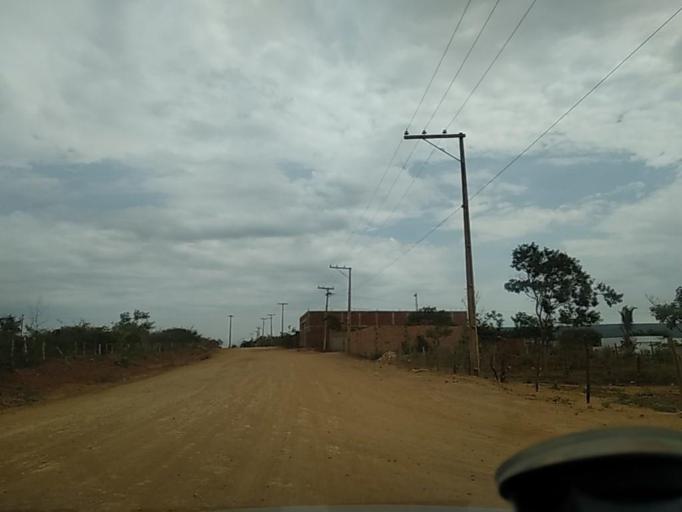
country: BR
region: Bahia
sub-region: Caetite
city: Caetite
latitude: -14.0504
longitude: -42.4734
